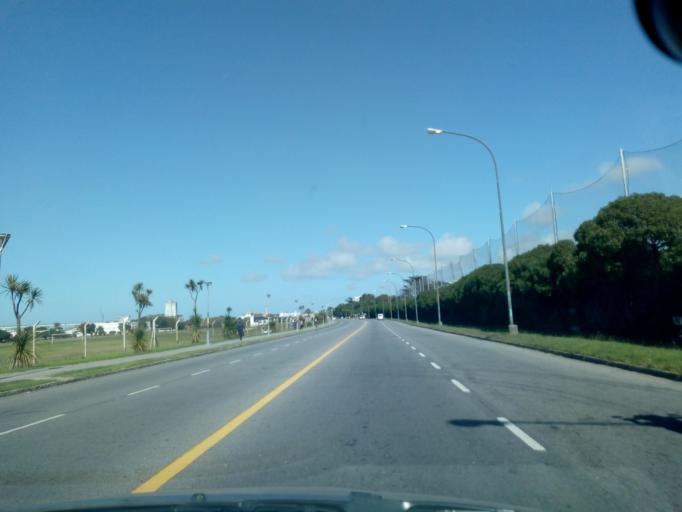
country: AR
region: Buenos Aires
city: Mar del Plata
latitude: -38.0335
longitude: -57.5363
